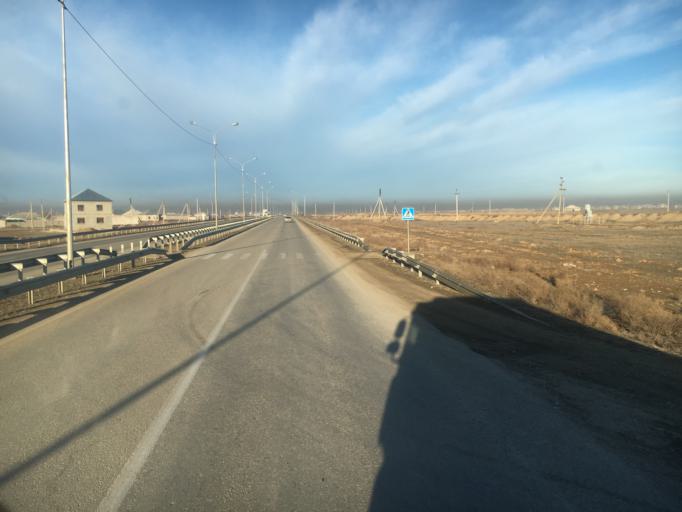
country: KZ
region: Ongtustik Qazaqstan
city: Turkestan
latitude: 43.3028
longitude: 68.3318
